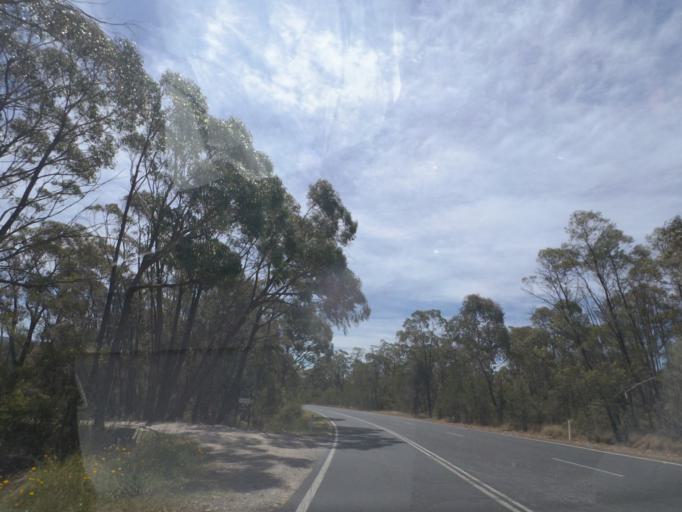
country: AU
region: New South Wales
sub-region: Wingecarribee
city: Colo Vale
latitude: -34.3957
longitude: 150.5331
